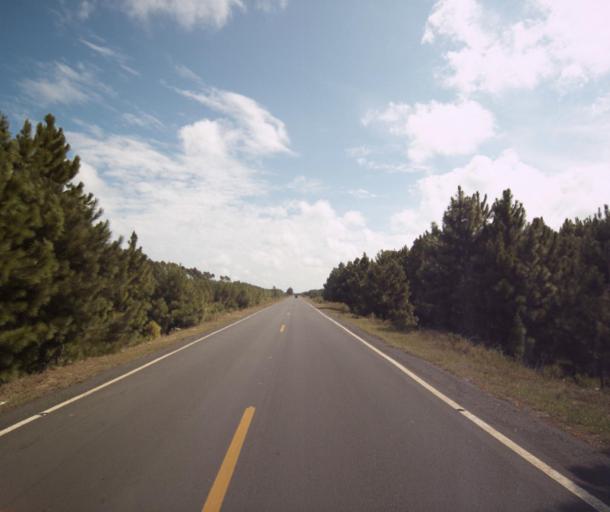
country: BR
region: Rio Grande do Sul
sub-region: Sao Lourenco Do Sul
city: Sao Lourenco do Sul
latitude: -31.4462
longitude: -51.2061
